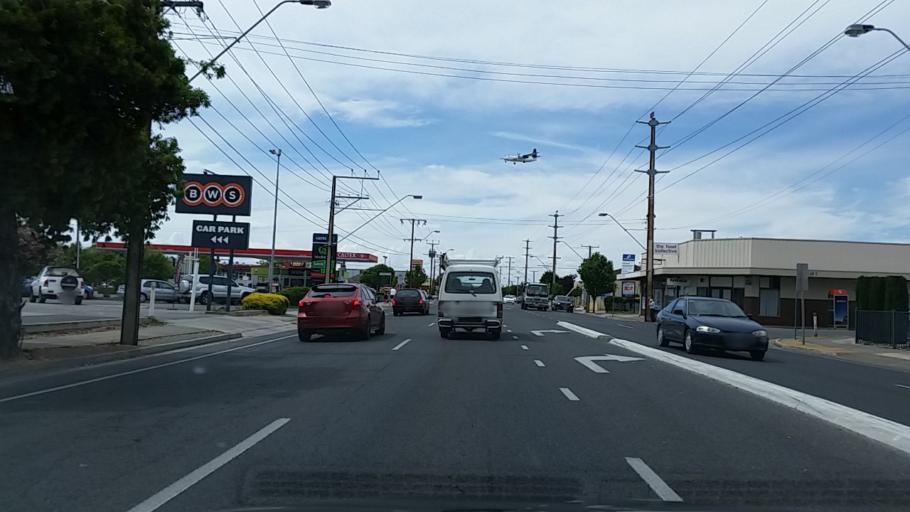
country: AU
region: South Australia
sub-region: City of West Torrens
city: Plympton
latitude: -34.9375
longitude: 138.5528
